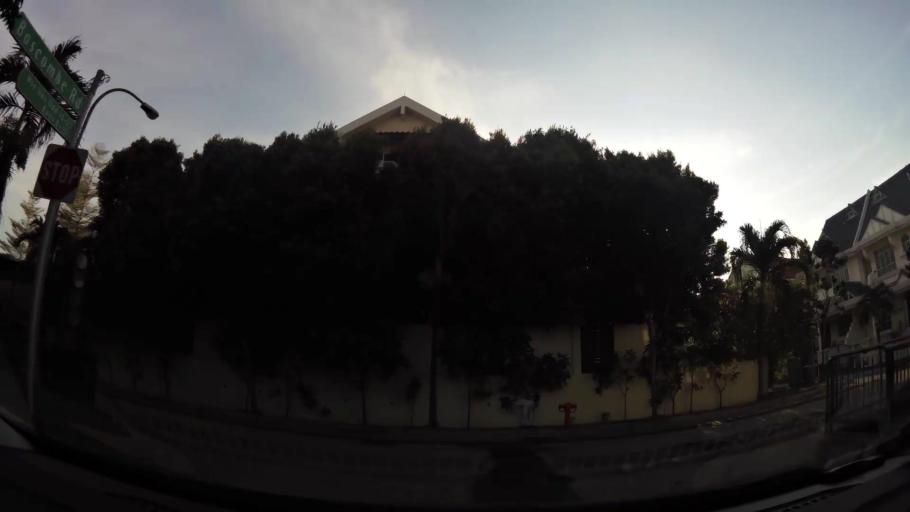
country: SG
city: Singapore
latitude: 1.3058
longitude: 103.8949
